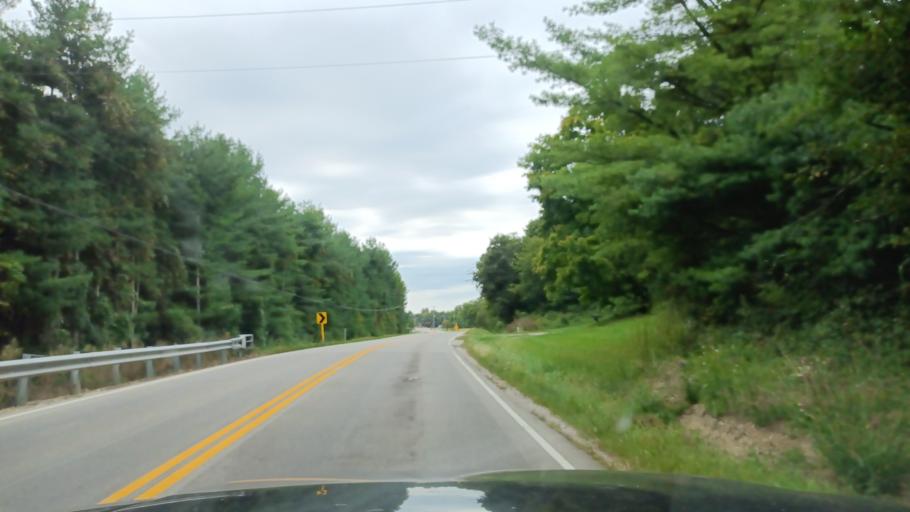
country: US
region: Ohio
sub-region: Ross County
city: Chillicothe
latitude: 39.2847
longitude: -82.8619
